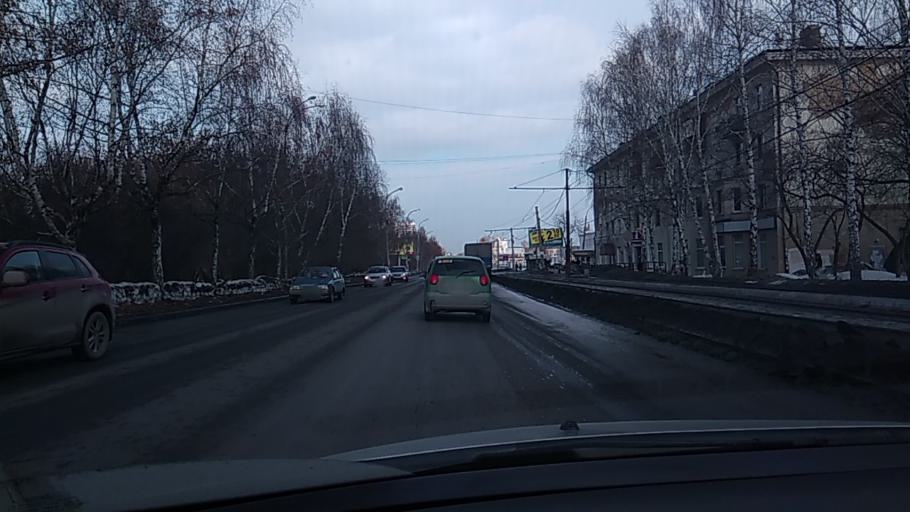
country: RU
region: Sverdlovsk
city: Yekaterinburg
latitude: 56.8576
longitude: 60.6544
